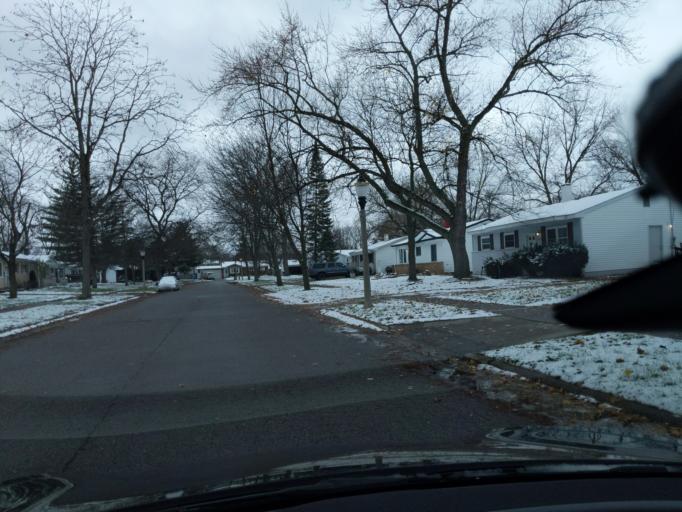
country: US
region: Michigan
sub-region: Eaton County
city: Waverly
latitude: 42.6844
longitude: -84.5993
